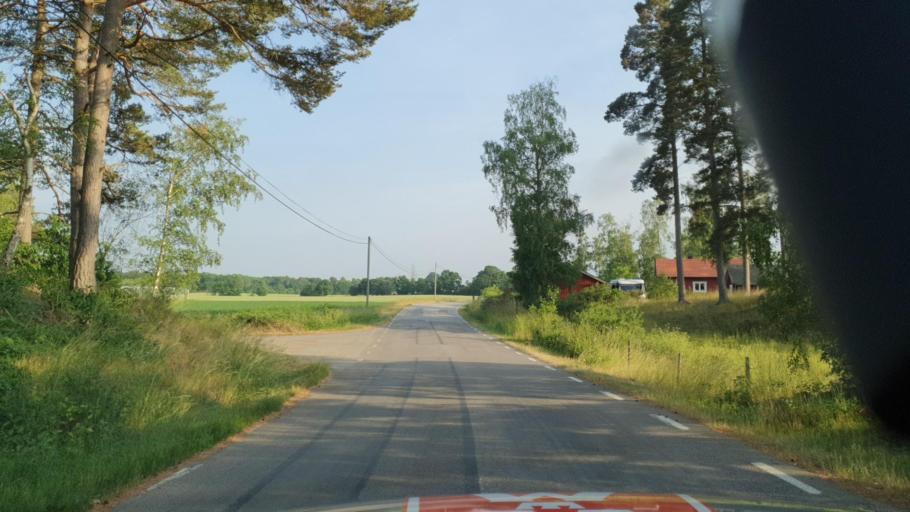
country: SE
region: Kalmar
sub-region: Torsas Kommun
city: Torsas
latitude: 56.4759
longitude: 16.0903
